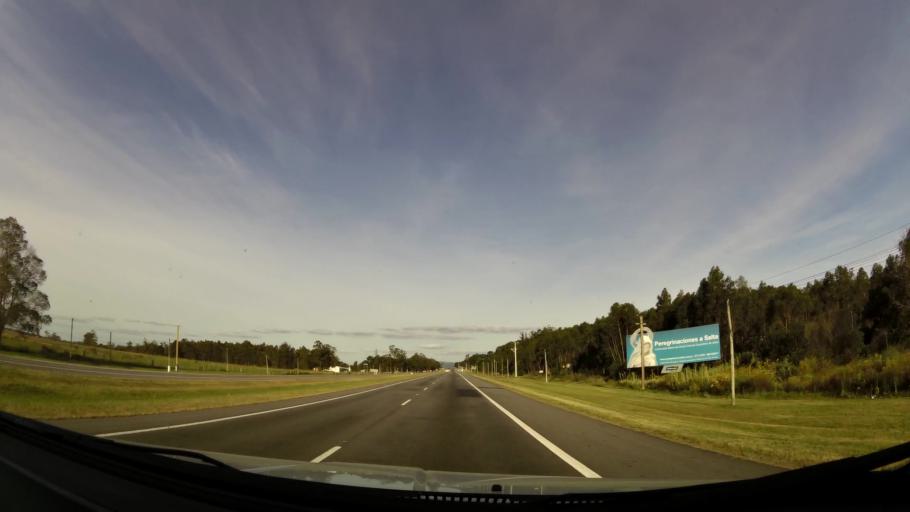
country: UY
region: Canelones
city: La Floresta
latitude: -34.7866
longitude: -55.5094
